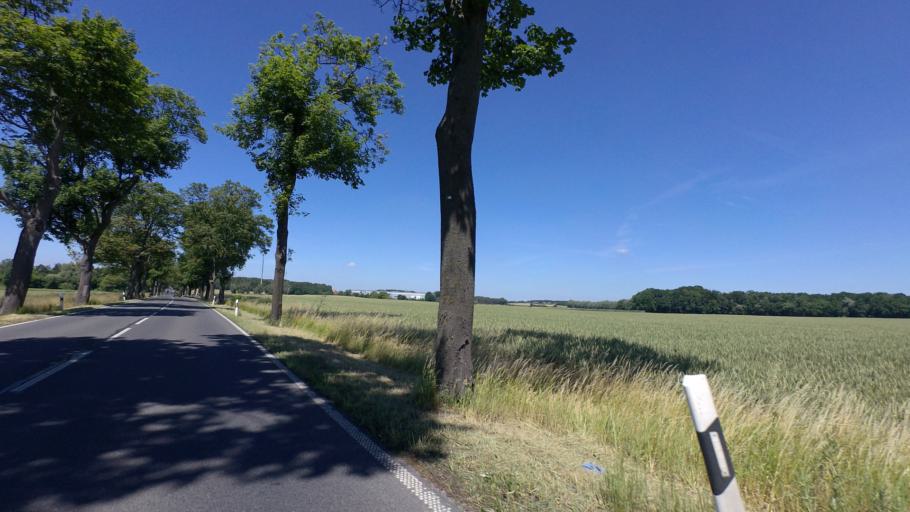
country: DE
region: Brandenburg
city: Rangsdorf
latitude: 52.2849
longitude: 13.4625
